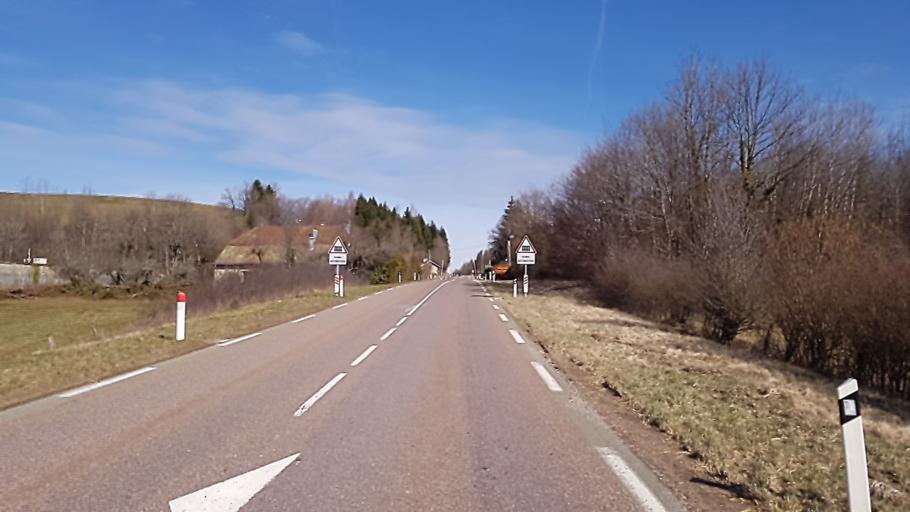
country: FR
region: Franche-Comte
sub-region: Departement du Jura
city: Champagnole
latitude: 46.6832
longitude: 5.9305
